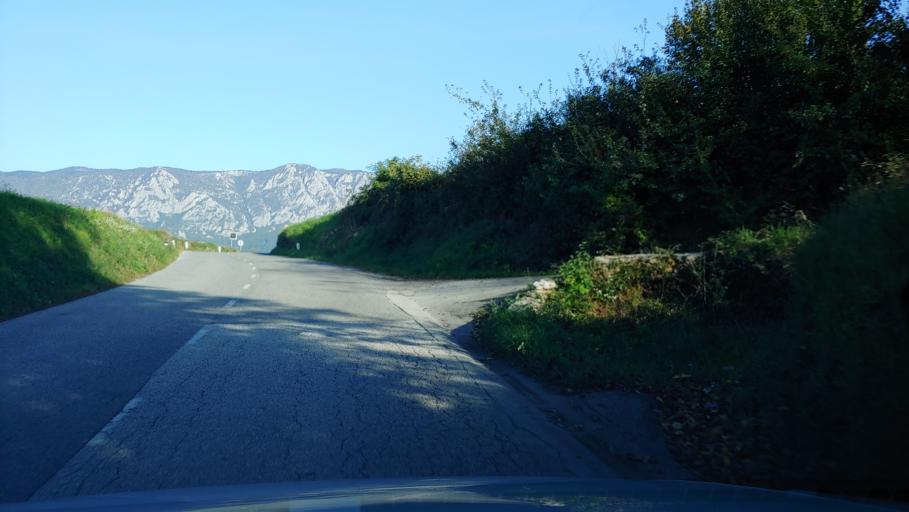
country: SI
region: Vipava
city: Vipava
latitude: 45.8144
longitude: 13.9212
